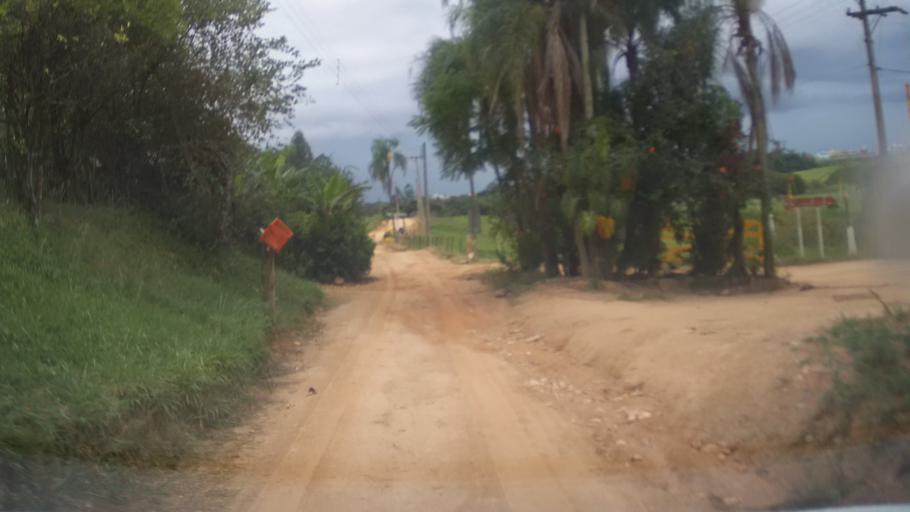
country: BR
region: Sao Paulo
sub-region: Itupeva
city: Itupeva
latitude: -23.1859
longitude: -47.0588
